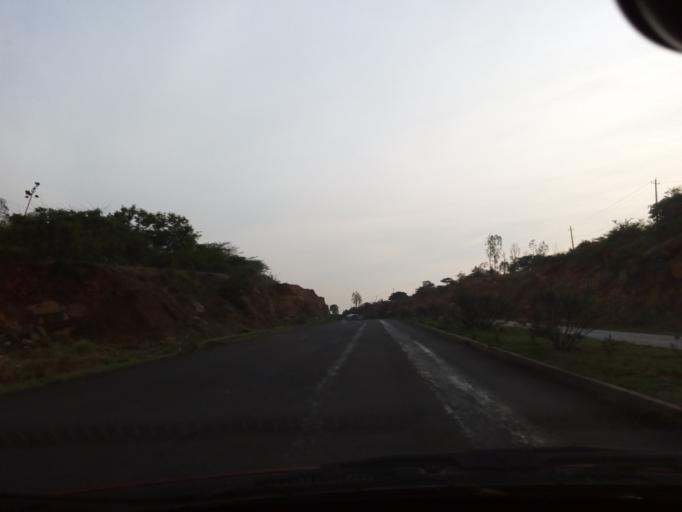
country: IN
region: Karnataka
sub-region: Chikkaballapur
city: Chik Ballapur
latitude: 13.5524
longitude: 77.7764
